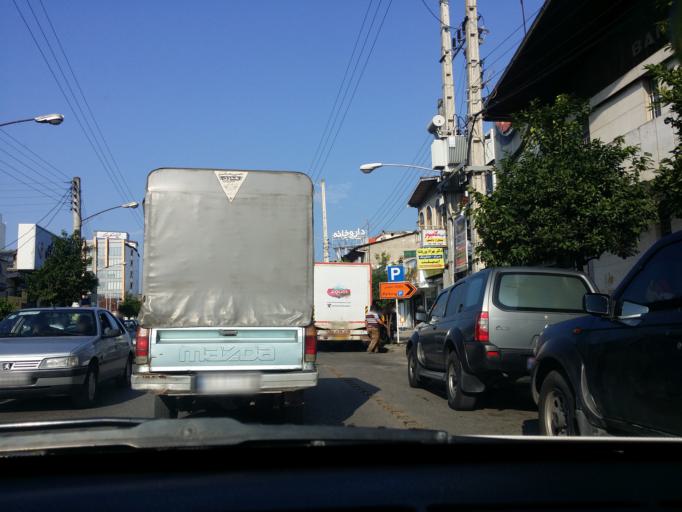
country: IR
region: Mazandaran
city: Chalus
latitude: 36.6561
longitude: 51.4186
